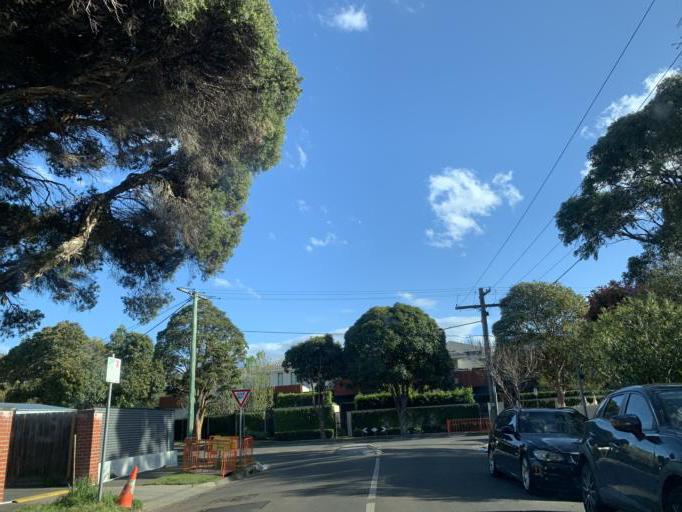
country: AU
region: Victoria
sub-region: Bayside
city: North Brighton
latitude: -37.9041
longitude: 145.0047
